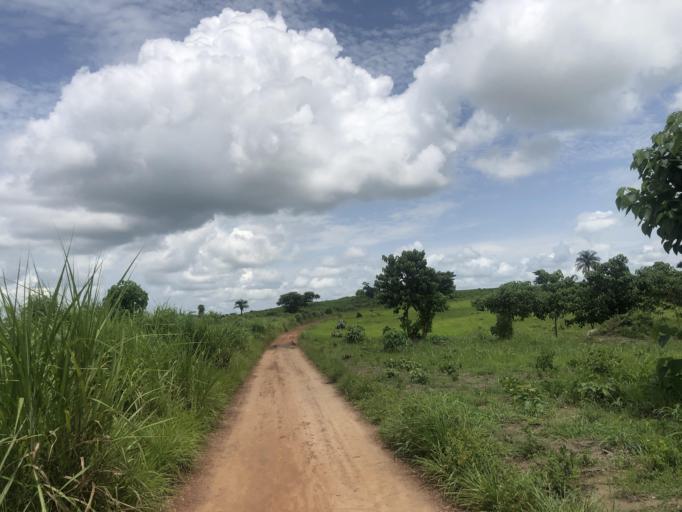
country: SL
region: Northern Province
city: Magburaka
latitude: 8.6926
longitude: -11.9433
